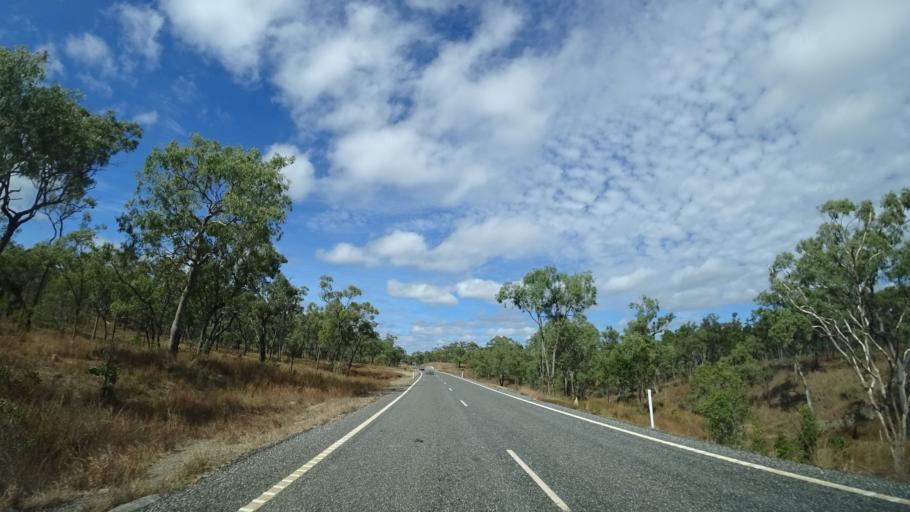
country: AU
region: Queensland
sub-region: Cairns
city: Port Douglas
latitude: -16.3305
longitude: 144.7216
